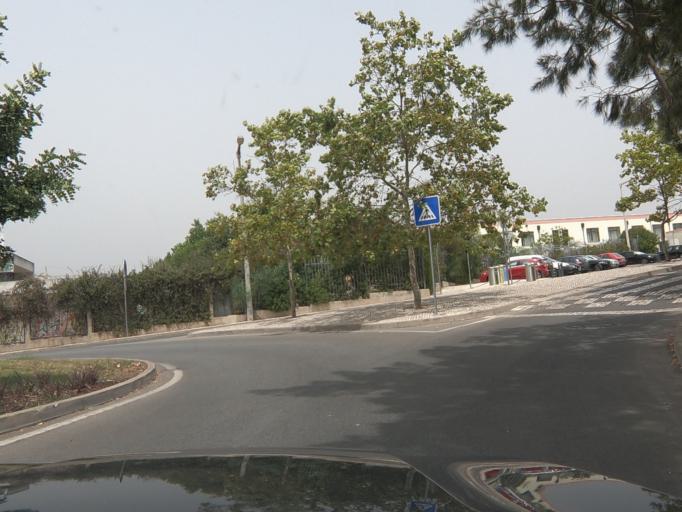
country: PT
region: Faro
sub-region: Portimao
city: Portimao
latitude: 37.1251
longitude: -8.5421
